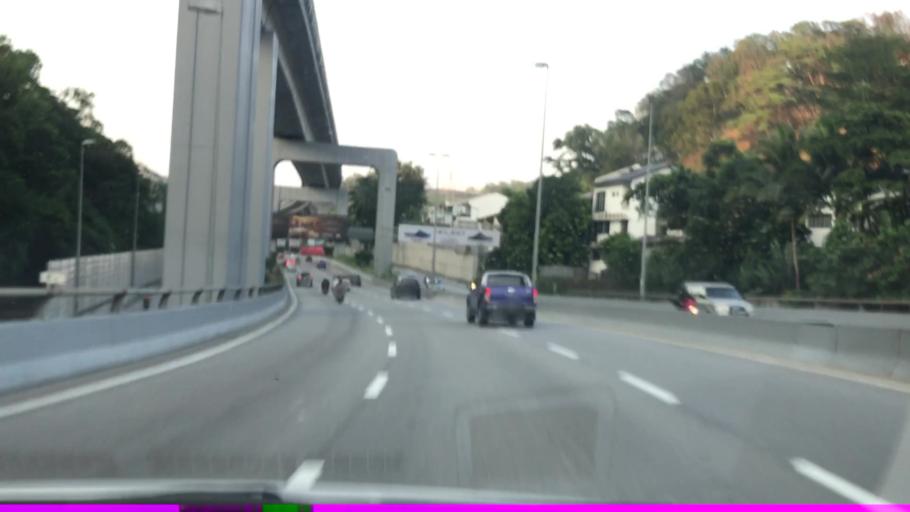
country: MY
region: Kuala Lumpur
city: Kuala Lumpur
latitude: 3.1428
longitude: 101.6610
